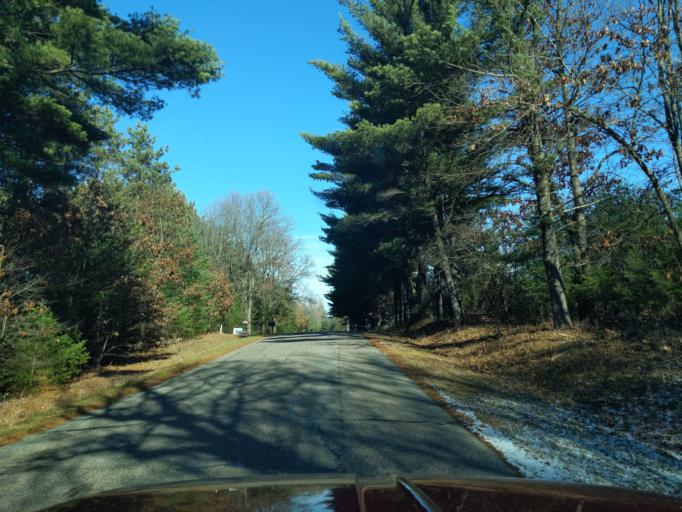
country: US
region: Wisconsin
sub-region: Waushara County
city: Silver Lake
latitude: 44.0797
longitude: -89.1939
